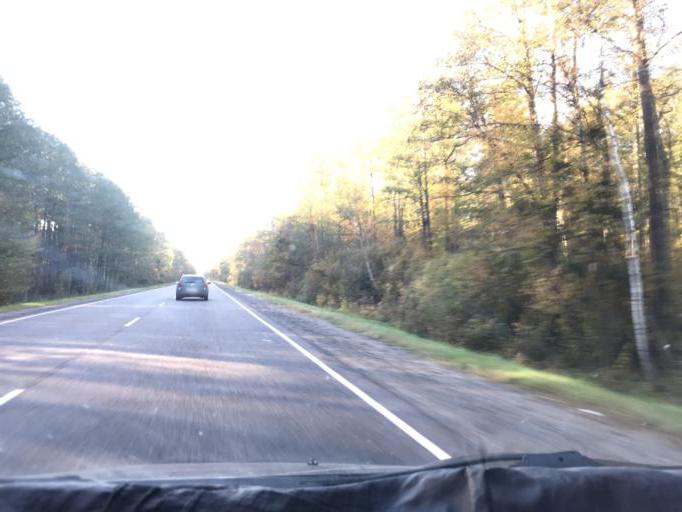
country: BY
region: Gomel
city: Pyetrykaw
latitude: 52.2685
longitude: 28.2884
